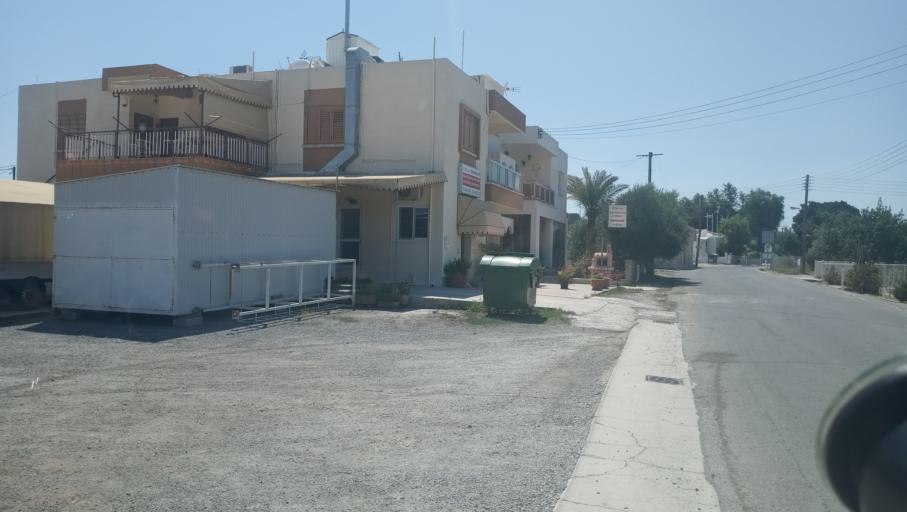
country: CY
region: Lefkosia
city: Psimolofou
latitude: 35.0630
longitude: 33.2595
